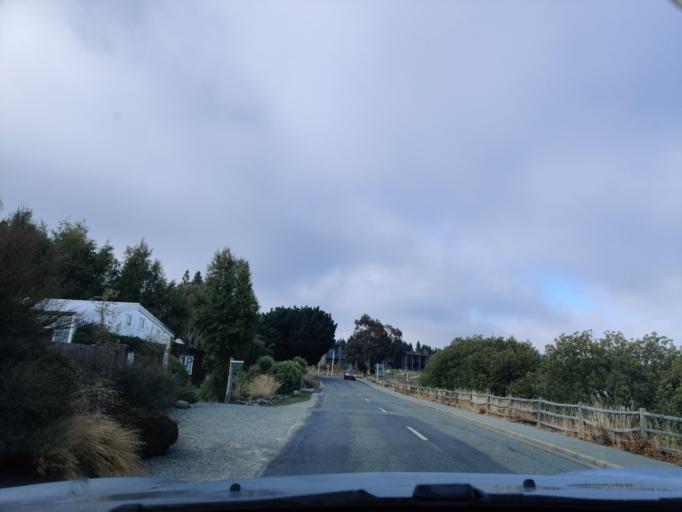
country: NZ
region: Canterbury
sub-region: Timaru District
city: Pleasant Point
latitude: -44.0056
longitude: 170.4818
